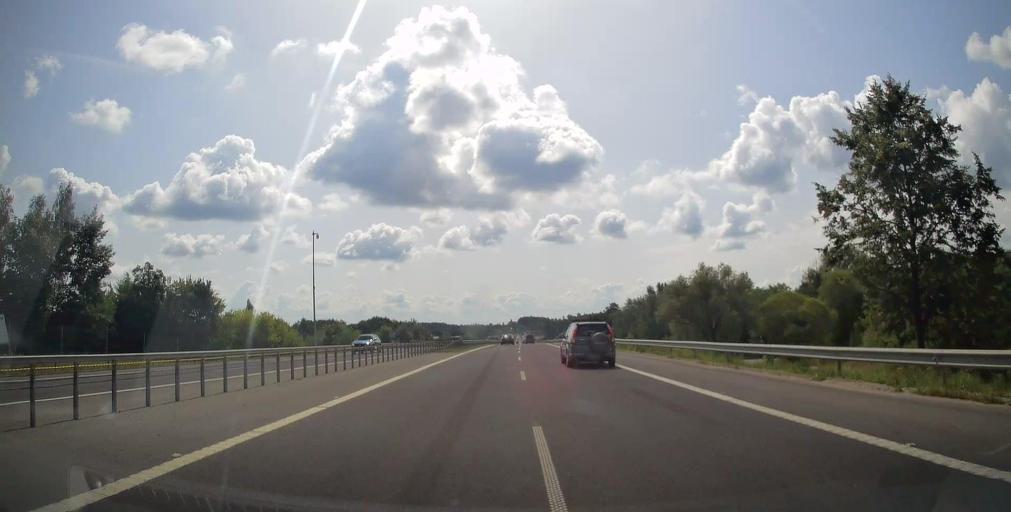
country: PL
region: Masovian Voivodeship
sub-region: Powiat grojecki
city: Grojec
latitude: 51.9065
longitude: 20.8576
